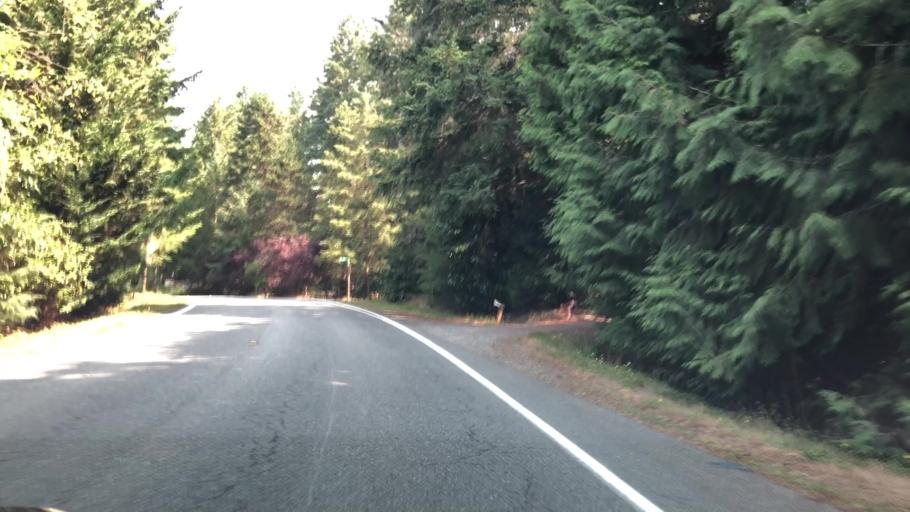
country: US
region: Washington
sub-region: King County
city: Cottage Lake
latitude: 47.7571
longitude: -122.0779
